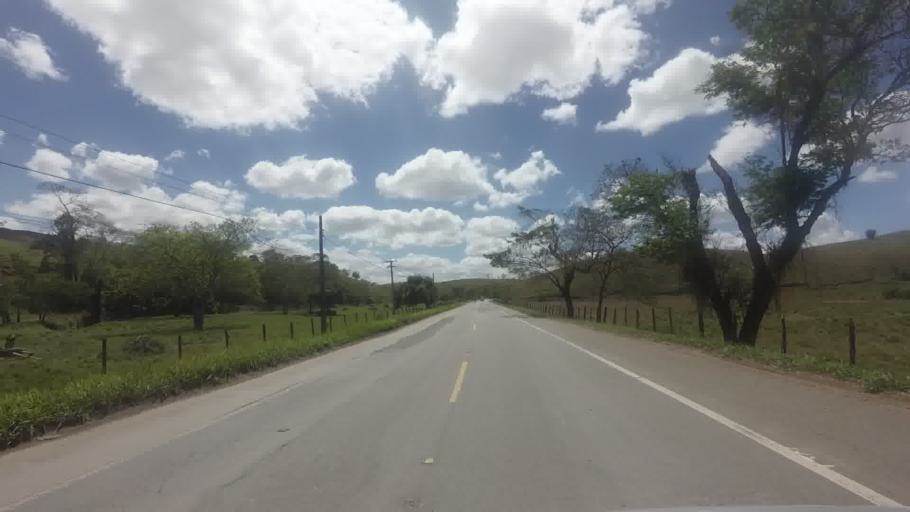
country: BR
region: Rio de Janeiro
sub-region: Santo Antonio De Padua
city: Santo Antonio de Padua
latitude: -21.6511
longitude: -42.2950
